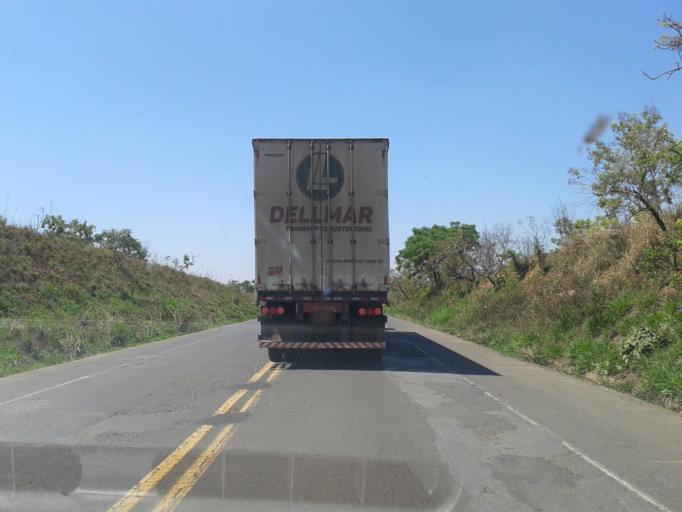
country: BR
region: Minas Gerais
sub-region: Araxa
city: Araxa
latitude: -19.4361
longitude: -47.1965
